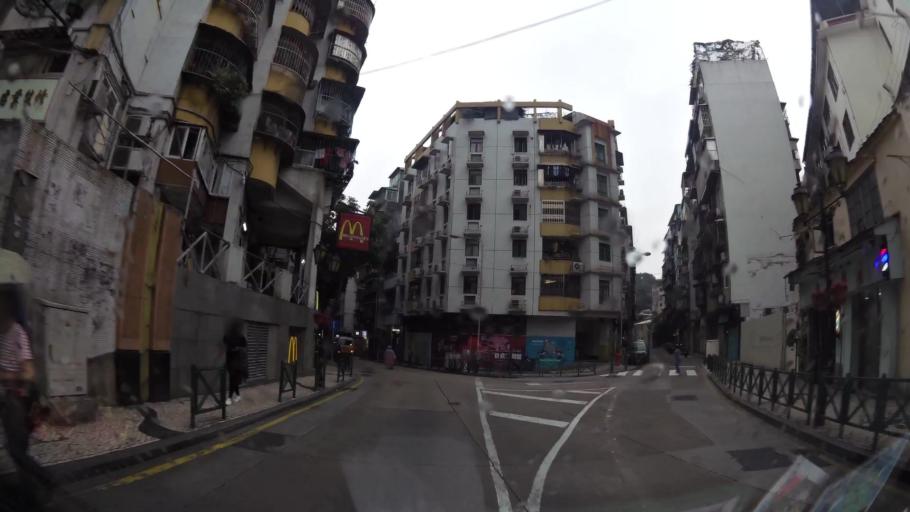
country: MO
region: Macau
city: Macau
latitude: 22.1992
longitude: 113.5400
